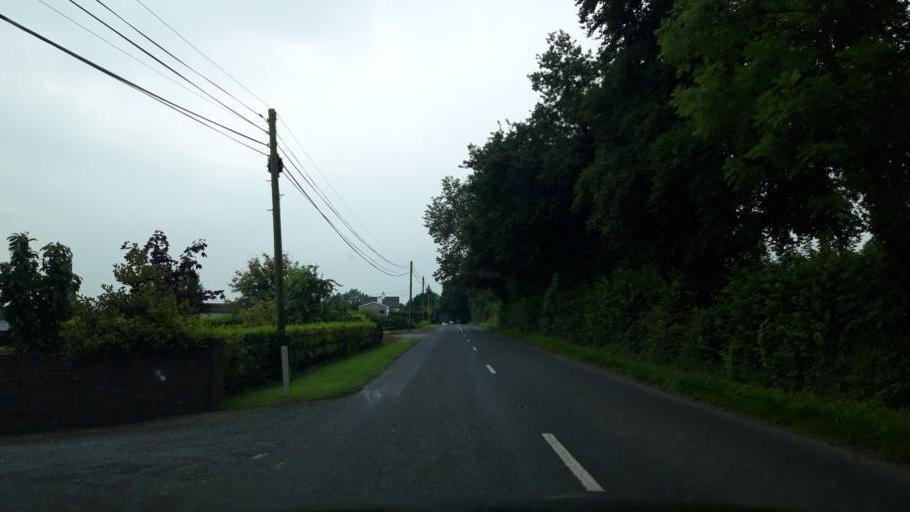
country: IE
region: Munster
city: Fethard
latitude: 52.5459
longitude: -7.6795
